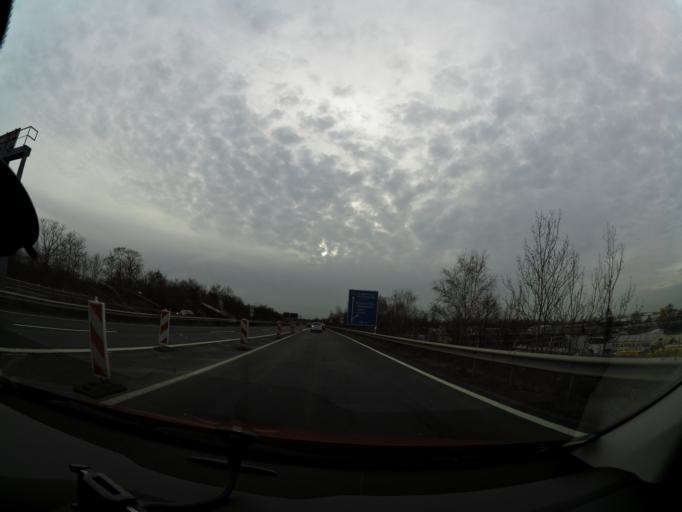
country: DE
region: Lower Saxony
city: Braunschweig
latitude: 52.3111
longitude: 10.5132
